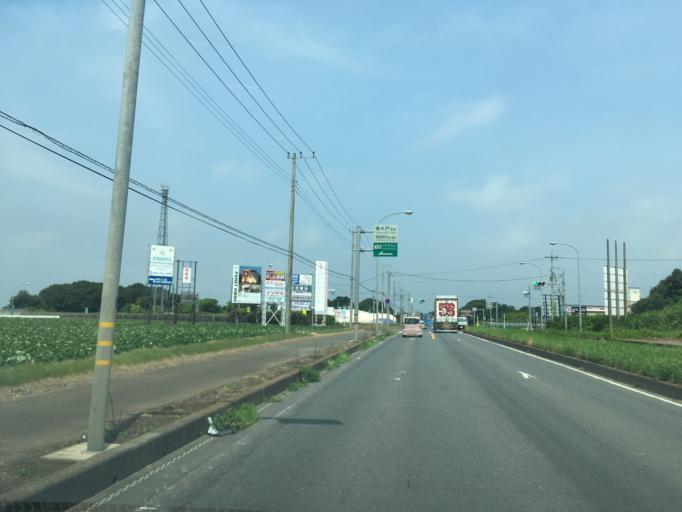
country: JP
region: Ibaraki
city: Katsuta
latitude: 36.3722
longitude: 140.5787
